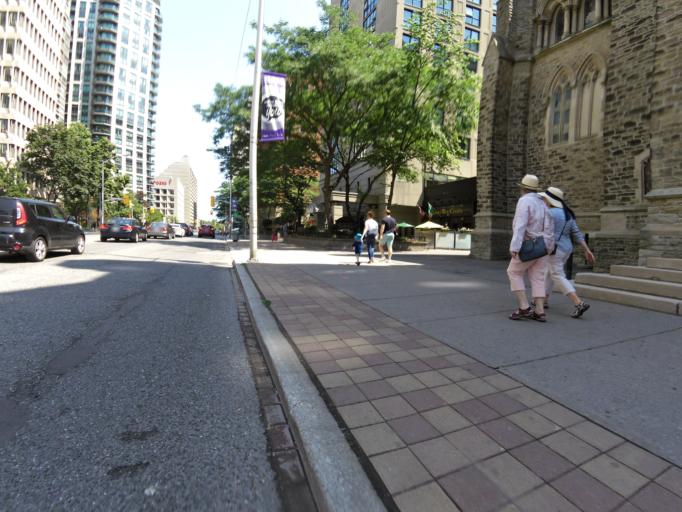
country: CA
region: Ontario
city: Toronto
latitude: 43.6715
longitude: -79.3813
